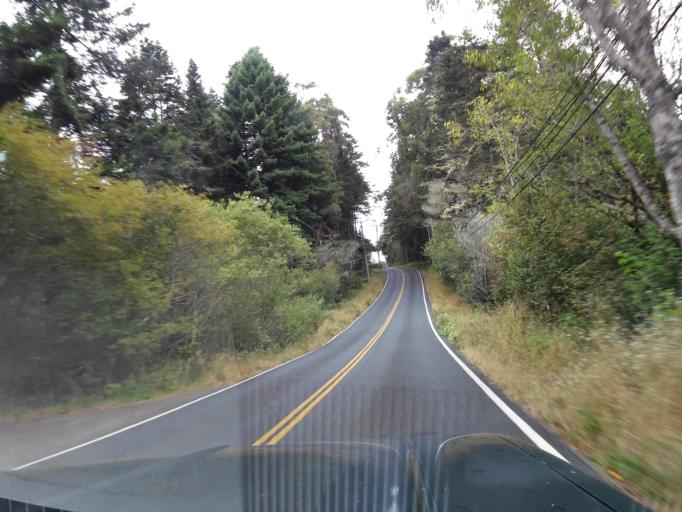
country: US
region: California
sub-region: Mendocino County
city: Fort Bragg
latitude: 39.3409
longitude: -123.8103
